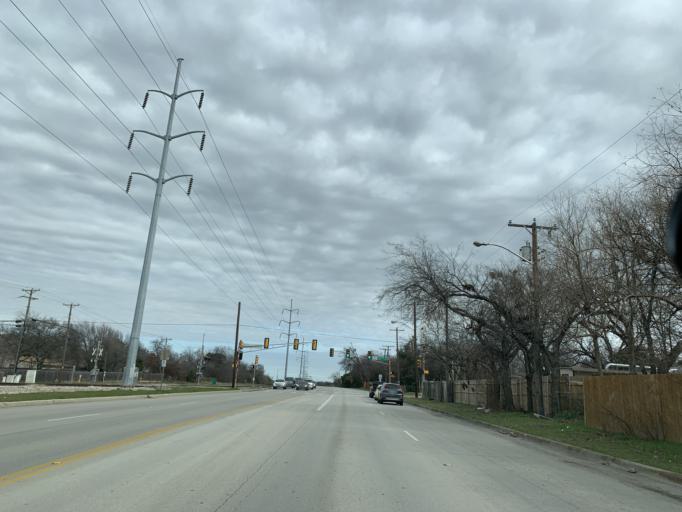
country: US
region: Texas
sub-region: Tarrant County
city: Edgecliff Village
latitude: 32.6777
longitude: -97.3775
